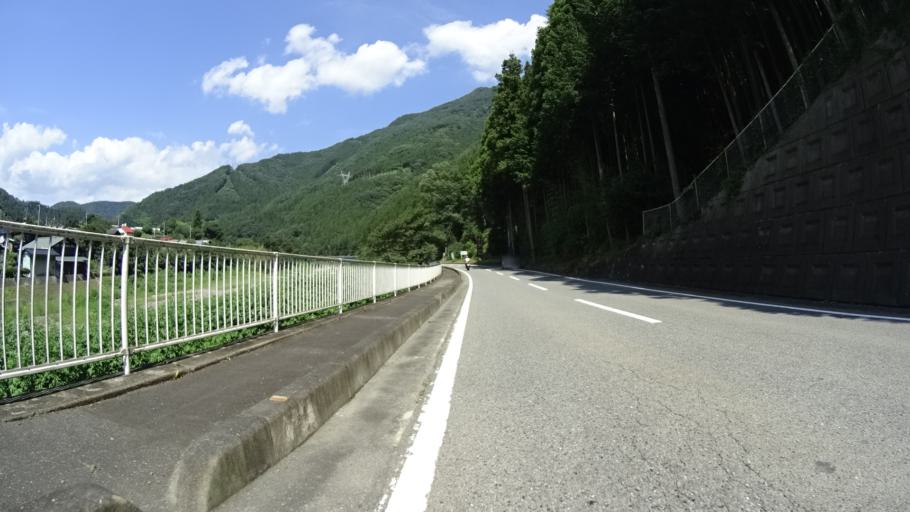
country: JP
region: Gunma
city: Tomioka
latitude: 36.0827
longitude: 138.7925
